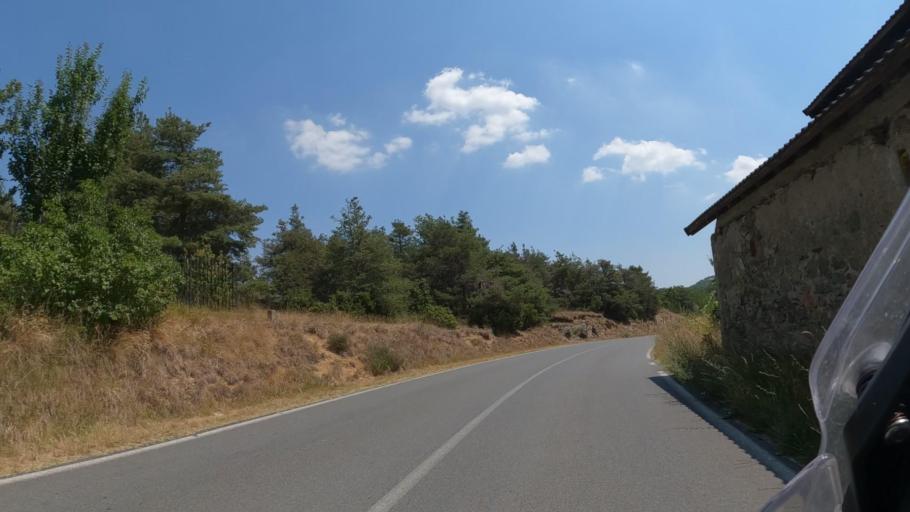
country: IT
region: Piedmont
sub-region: Provincia di Alessandria
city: Ponzone
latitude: 44.5558
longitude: 8.4949
